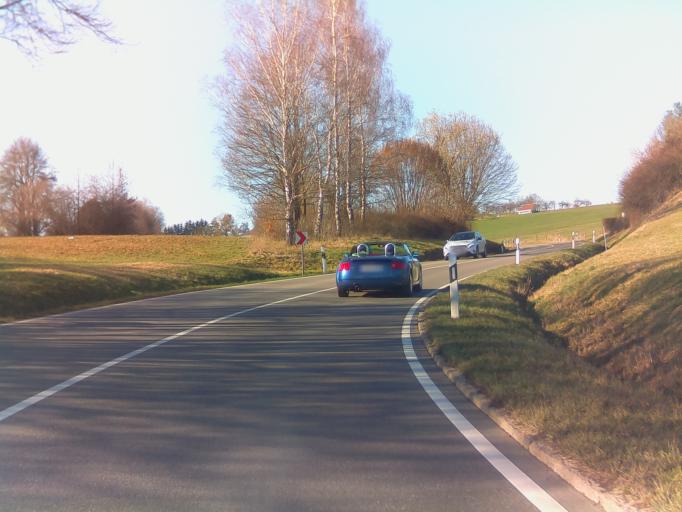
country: DE
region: Baden-Wuerttemberg
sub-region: Regierungsbezirk Stuttgart
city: Waldenbuch
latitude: 48.6468
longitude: 9.1334
